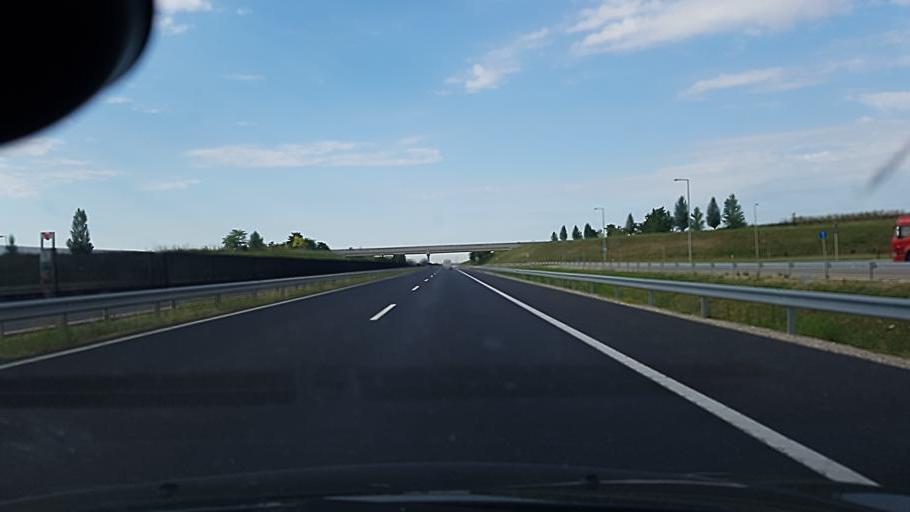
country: HU
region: Fejer
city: Rackeresztur
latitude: 47.2853
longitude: 18.8629
